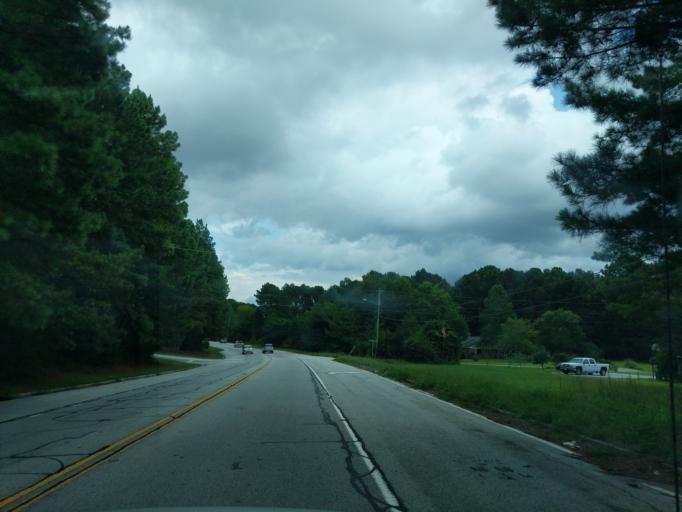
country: US
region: Georgia
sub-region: Walton County
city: Loganville
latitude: 33.8178
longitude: -83.9267
